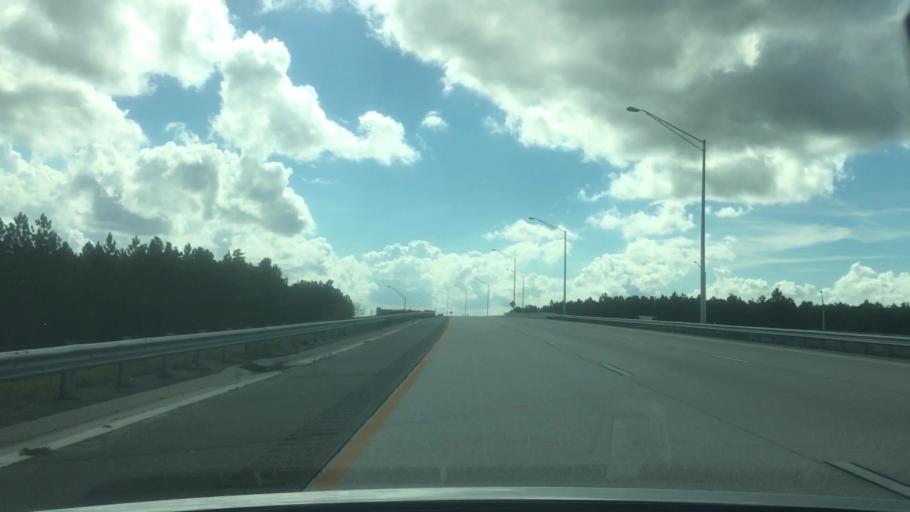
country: US
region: Florida
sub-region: Saint Johns County
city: Fruit Cove
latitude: 30.1198
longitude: -81.5136
